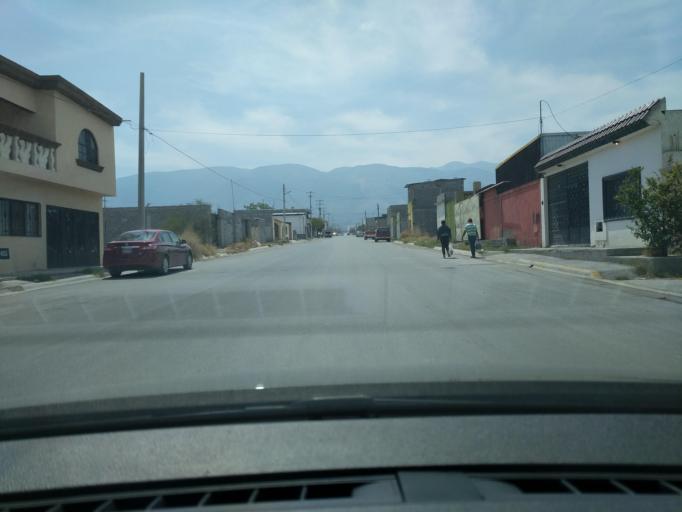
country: MX
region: Coahuila
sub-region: Arteaga
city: Arteaga
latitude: 25.4309
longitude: -100.9097
